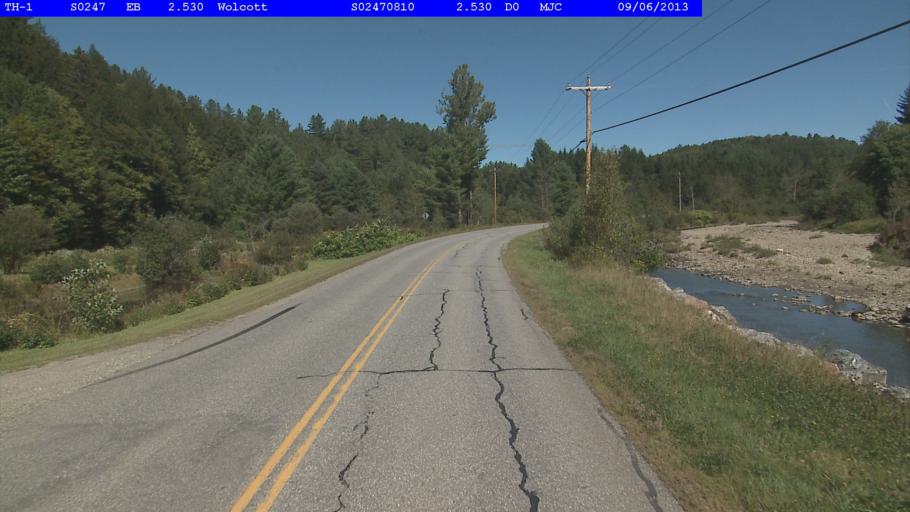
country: US
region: Vermont
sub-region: Lamoille County
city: Morrisville
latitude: 44.5919
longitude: -72.4742
